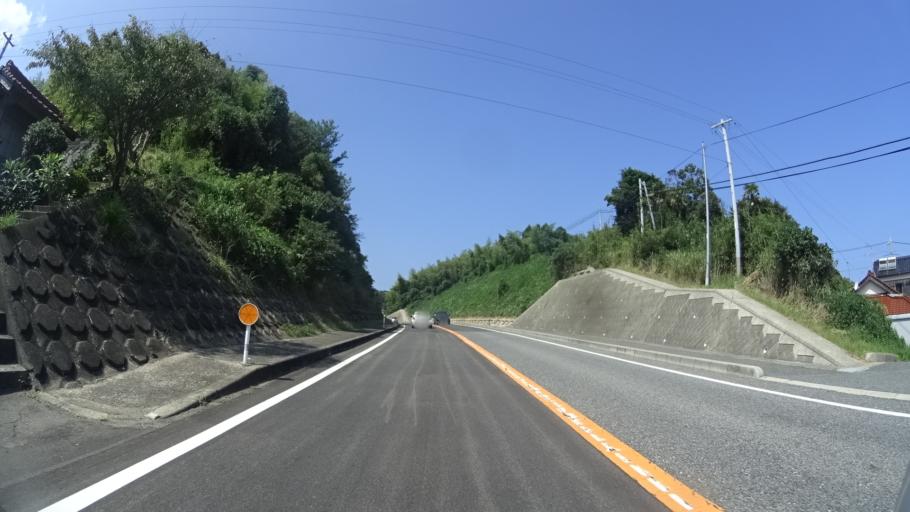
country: JP
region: Shimane
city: Masuda
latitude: 34.6717
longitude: 131.7382
